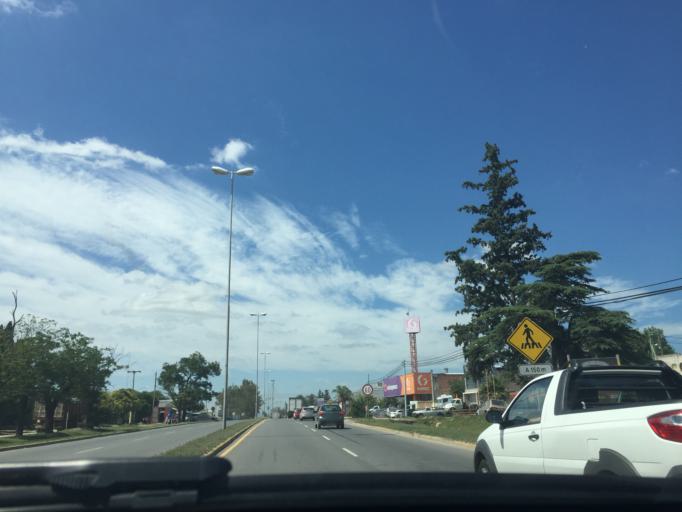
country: AR
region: Cordoba
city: Alta Gracia
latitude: -31.6560
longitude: -64.4092
